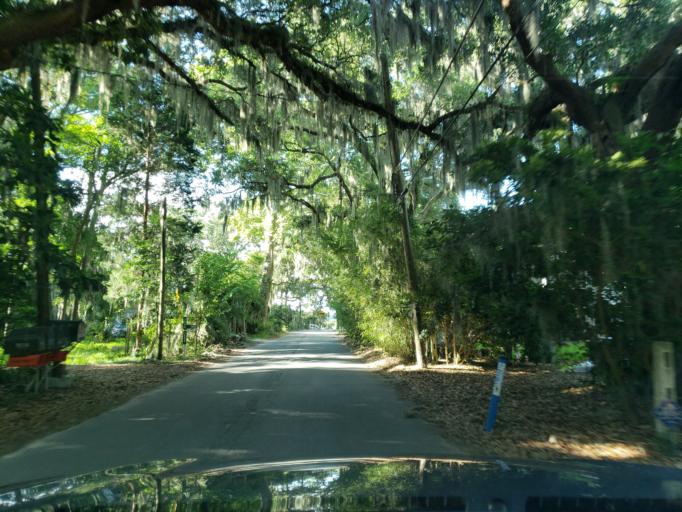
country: US
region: Georgia
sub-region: Chatham County
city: Isle of Hope
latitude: 31.9839
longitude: -81.0538
